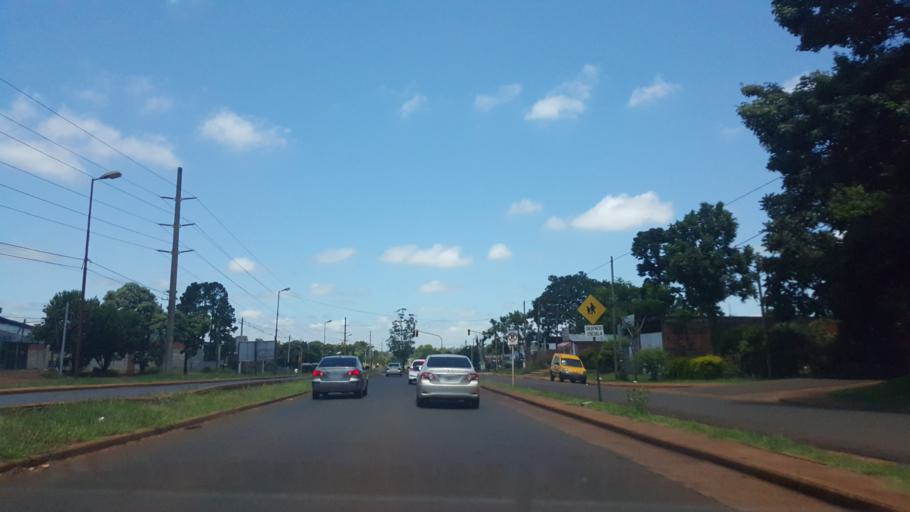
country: AR
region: Misiones
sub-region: Departamento de Capital
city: Posadas
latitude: -27.4115
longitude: -55.9266
